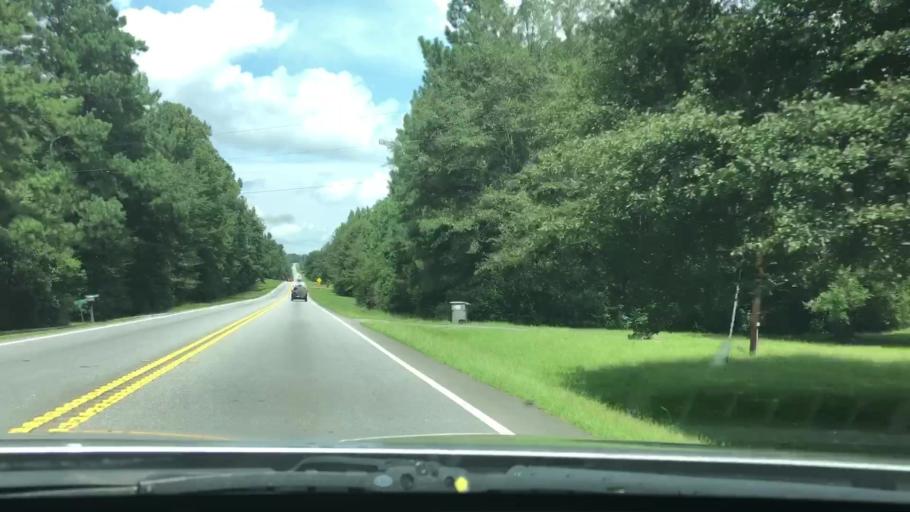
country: US
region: Georgia
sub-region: Lamar County
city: Barnesville
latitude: 33.1156
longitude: -84.1543
